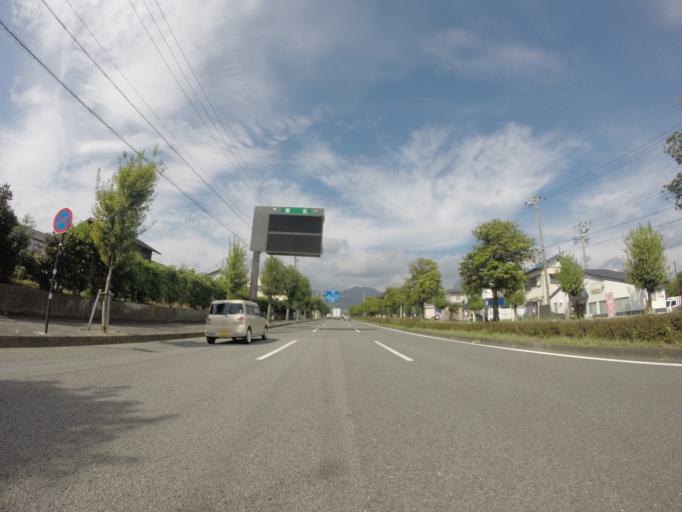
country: JP
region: Shizuoka
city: Shizuoka-shi
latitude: 35.0392
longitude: 138.4876
